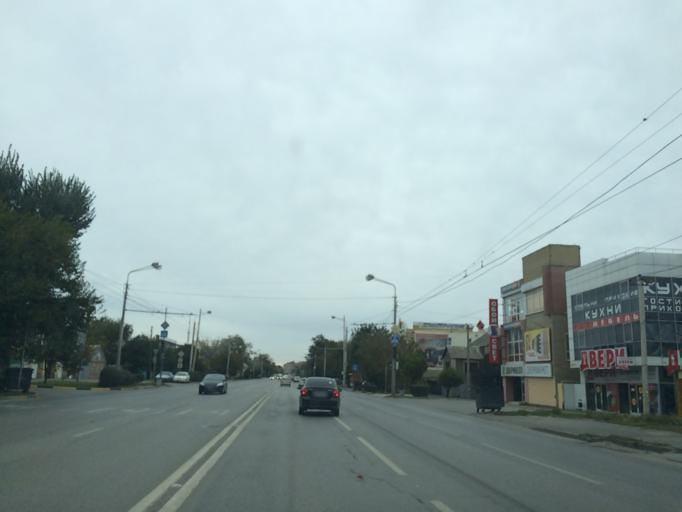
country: RU
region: Rostov
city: Rostov-na-Donu
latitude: 47.2119
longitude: 39.6516
